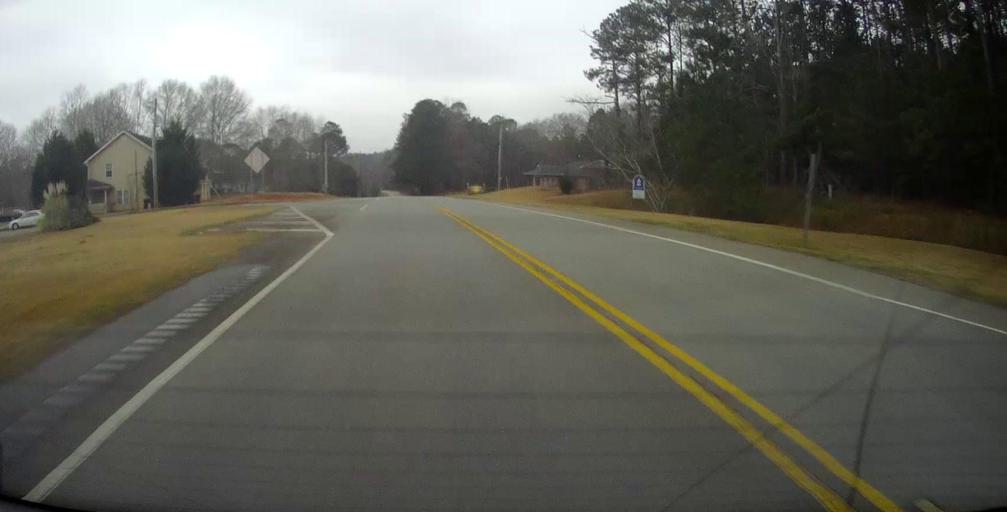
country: US
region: Georgia
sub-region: Lamar County
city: Barnesville
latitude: 33.0538
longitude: -84.1314
